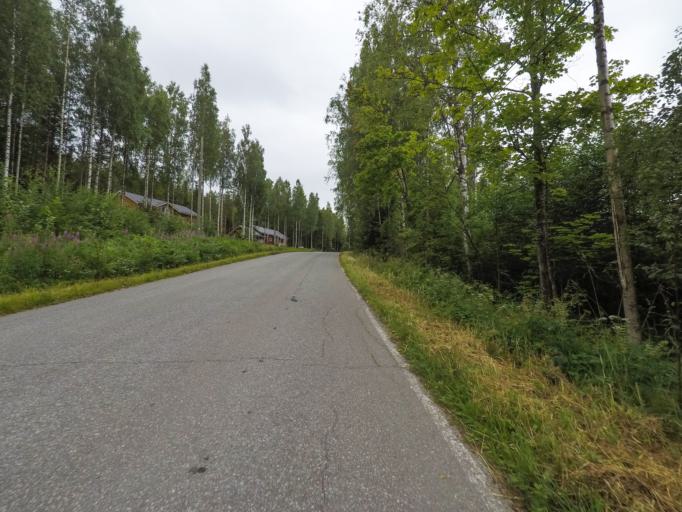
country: FI
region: Uusimaa
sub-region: Helsinki
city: Karjalohja
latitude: 60.2567
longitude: 23.7411
